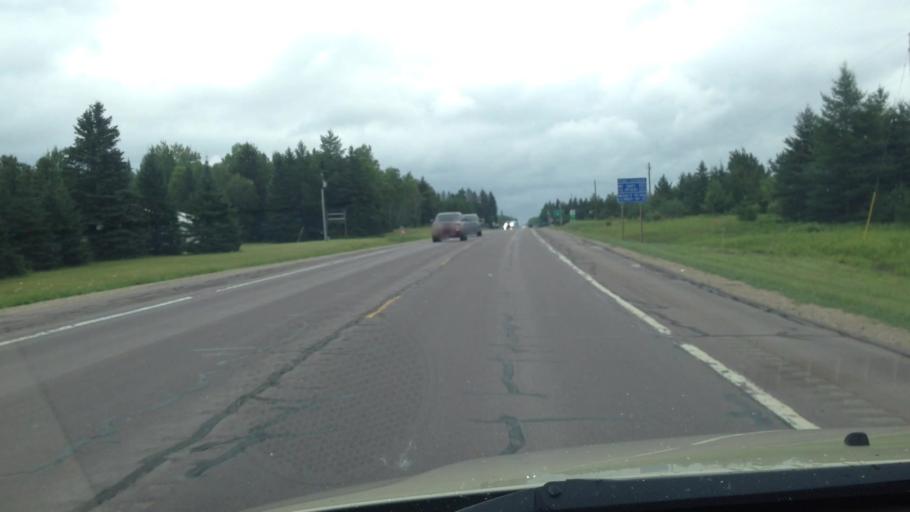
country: US
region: Michigan
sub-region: Schoolcraft County
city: Manistique
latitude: 46.1007
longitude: -85.9355
